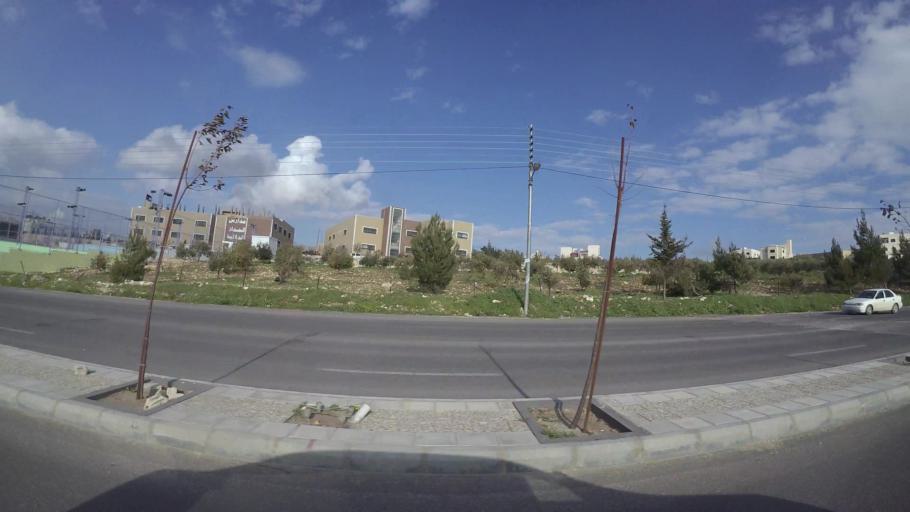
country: JO
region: Amman
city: Wadi as Sir
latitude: 31.9290
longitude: 35.8487
